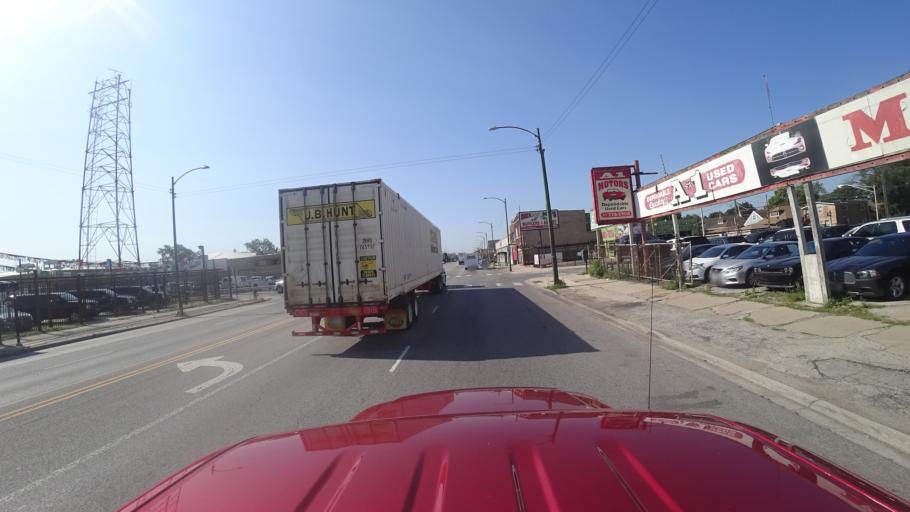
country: US
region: Illinois
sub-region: Cook County
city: Chicago
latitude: 41.7907
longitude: -87.6841
